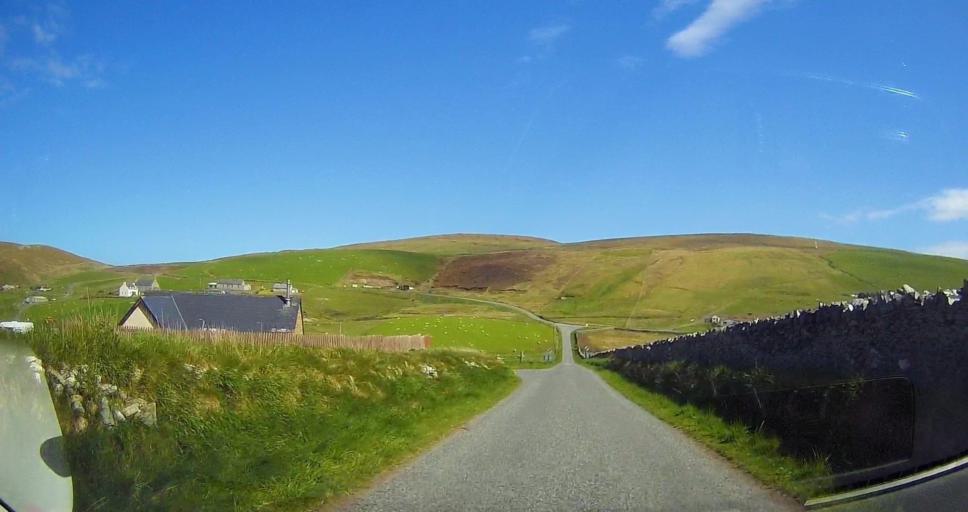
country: GB
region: Scotland
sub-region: Shetland Islands
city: Sandwick
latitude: 59.9728
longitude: -1.3211
